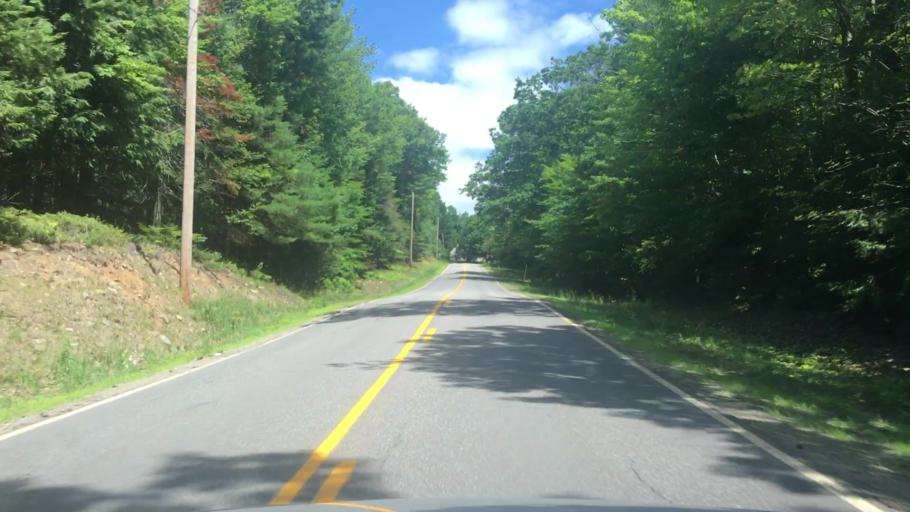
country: US
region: Maine
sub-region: Waldo County
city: Searsmont
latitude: 44.4447
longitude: -69.3061
